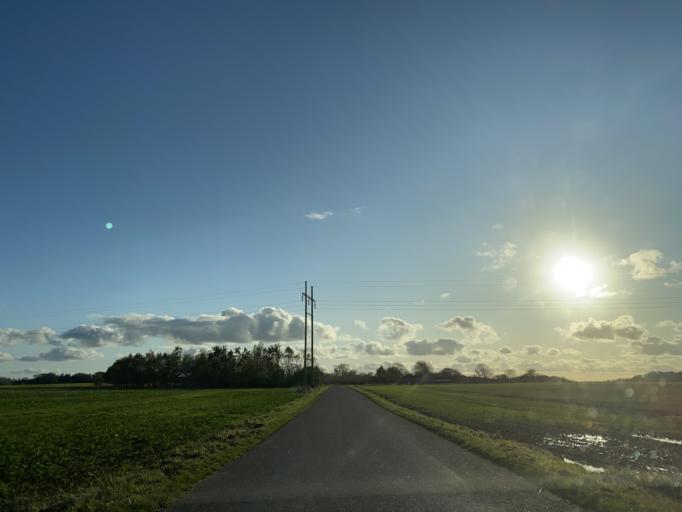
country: DK
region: Central Jutland
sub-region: Viborg Kommune
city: Bjerringbro
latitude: 56.3211
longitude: 9.7016
